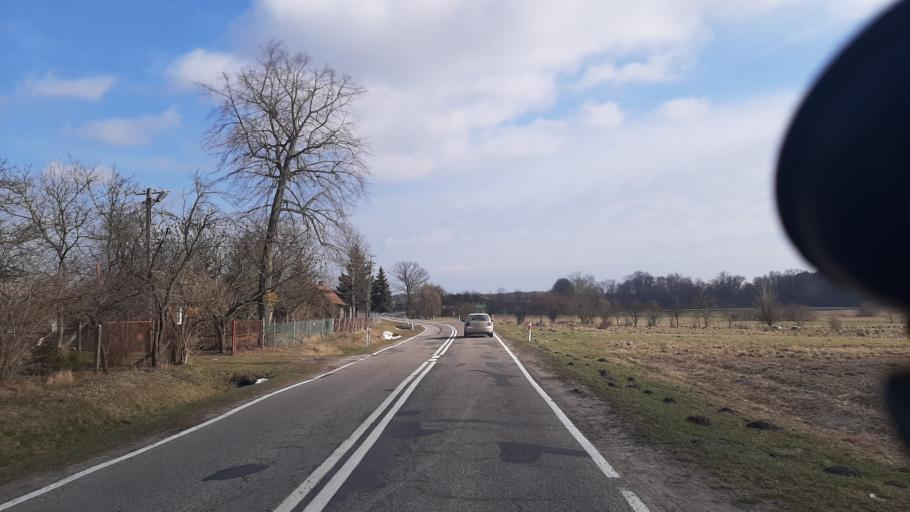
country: PL
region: Lublin Voivodeship
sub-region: Powiat parczewski
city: Sosnowica
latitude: 51.4980
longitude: 23.1639
